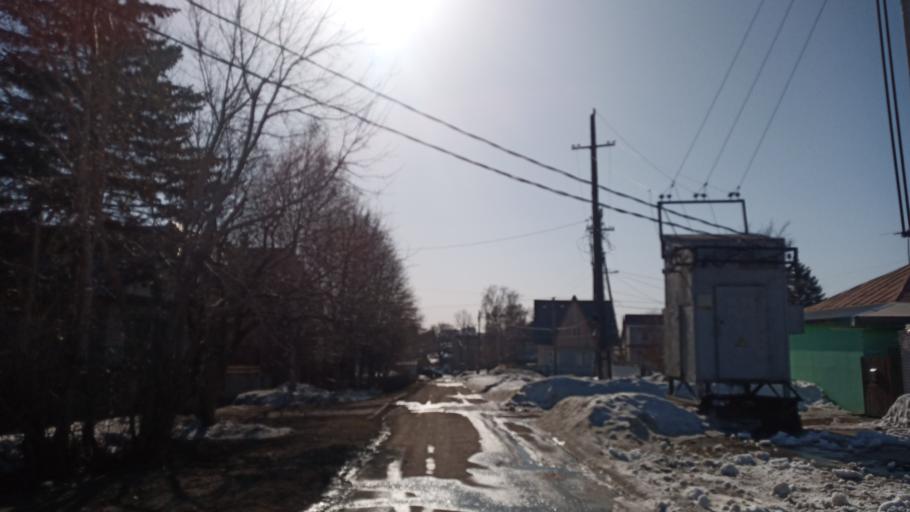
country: RU
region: Altai Krai
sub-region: Gorod Barnaulskiy
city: Barnaul
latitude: 53.3595
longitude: 83.7429
